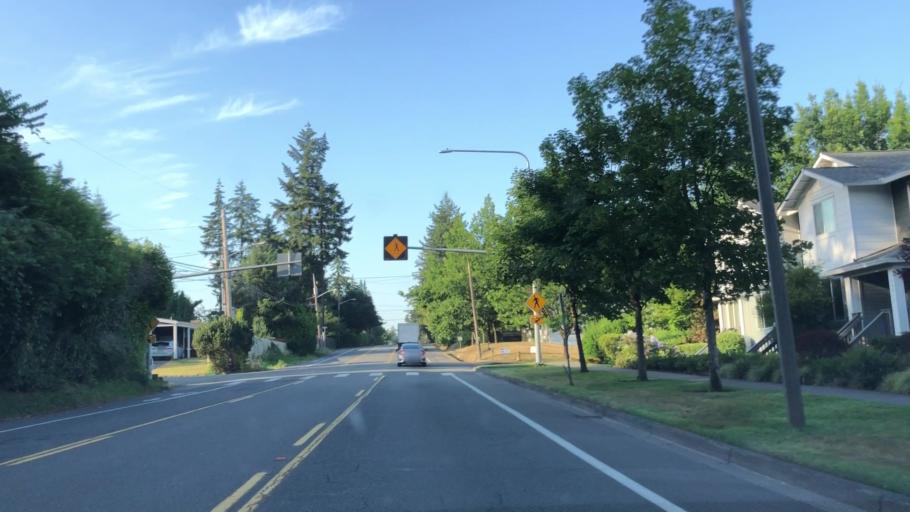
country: US
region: Washington
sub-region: King County
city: Kingsgate
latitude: 47.6982
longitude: -122.1758
